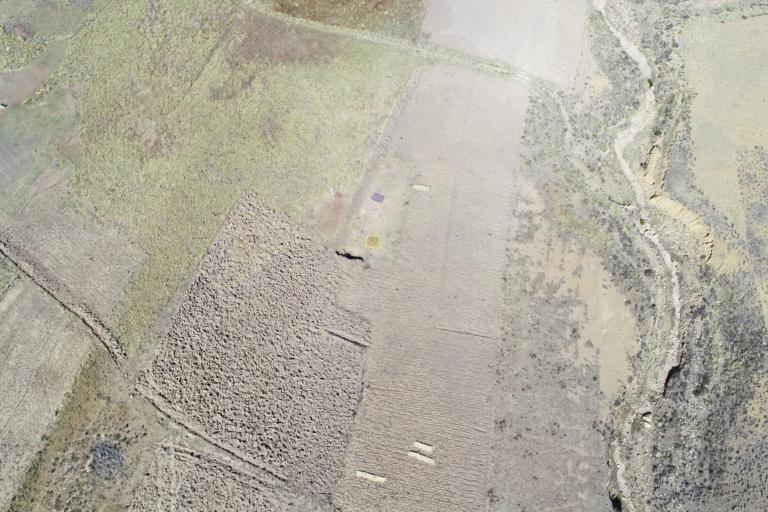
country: BO
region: La Paz
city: Achacachi
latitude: -15.8847
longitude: -68.8093
